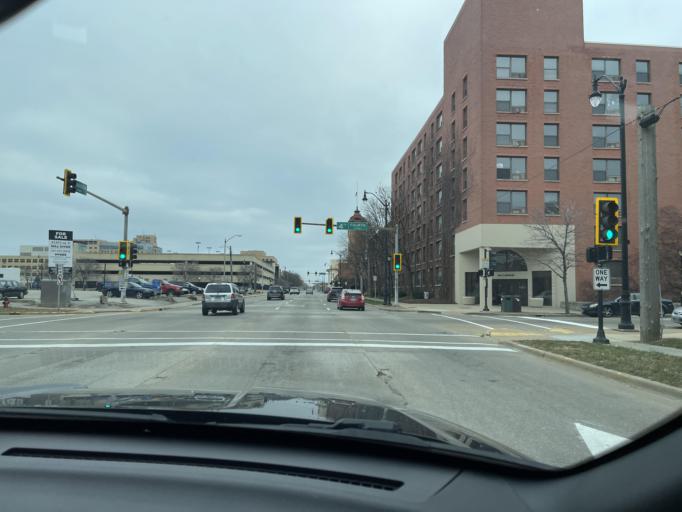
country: US
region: Illinois
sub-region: Sangamon County
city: Springfield
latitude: 39.8040
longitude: -89.6509
